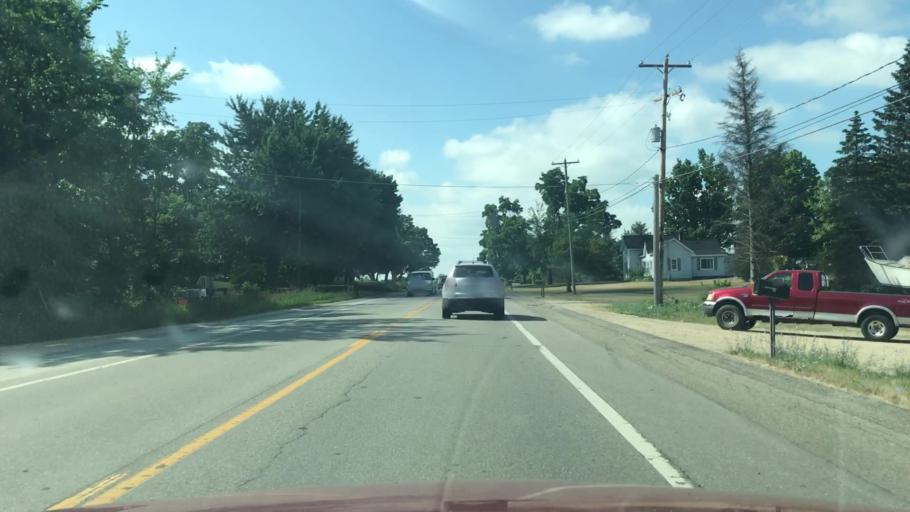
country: US
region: Michigan
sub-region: Newaygo County
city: Newaygo
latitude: 43.3176
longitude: -85.8107
